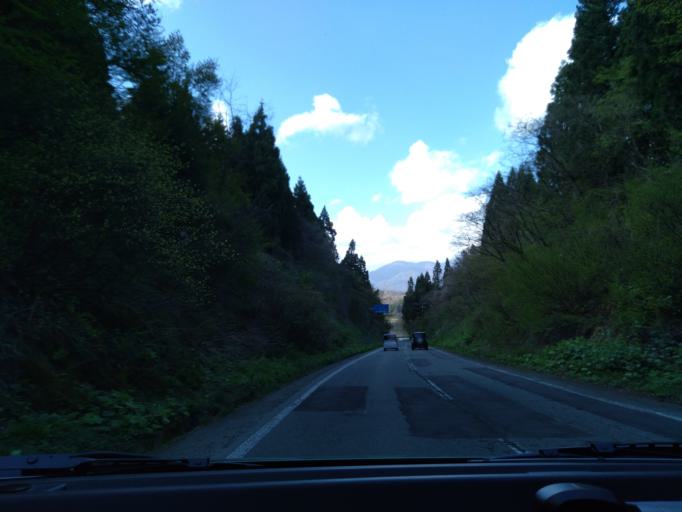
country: JP
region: Akita
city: Akita
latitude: 39.6906
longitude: 140.2748
